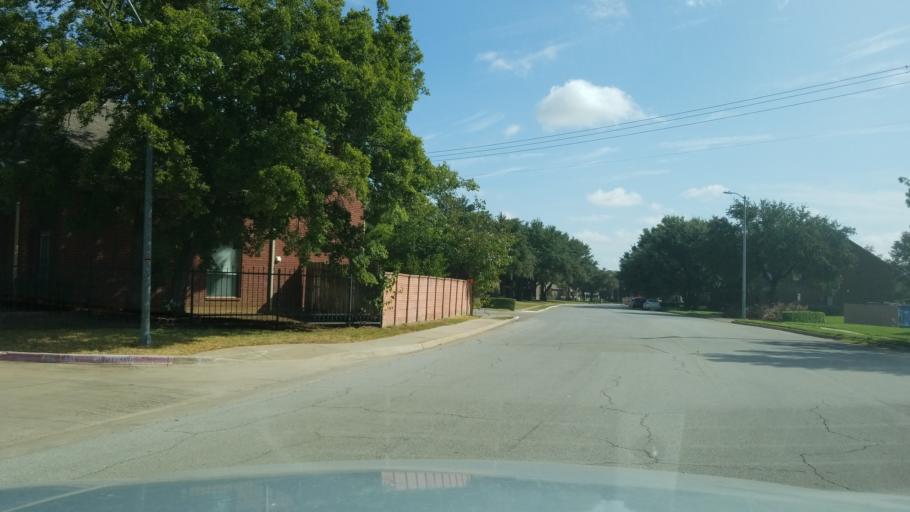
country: US
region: Texas
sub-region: Tarrant County
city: Euless
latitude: 32.8482
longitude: -97.0747
